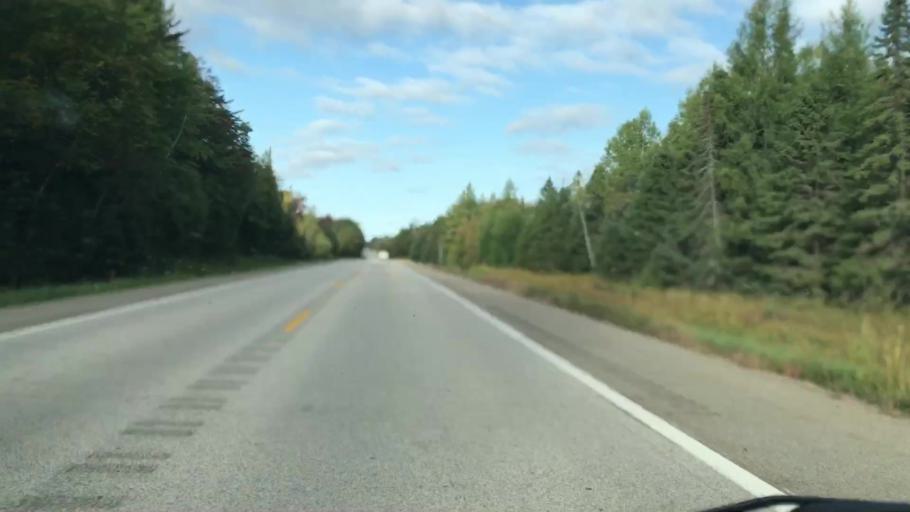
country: US
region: Michigan
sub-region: Luce County
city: Newberry
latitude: 46.3320
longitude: -85.0869
